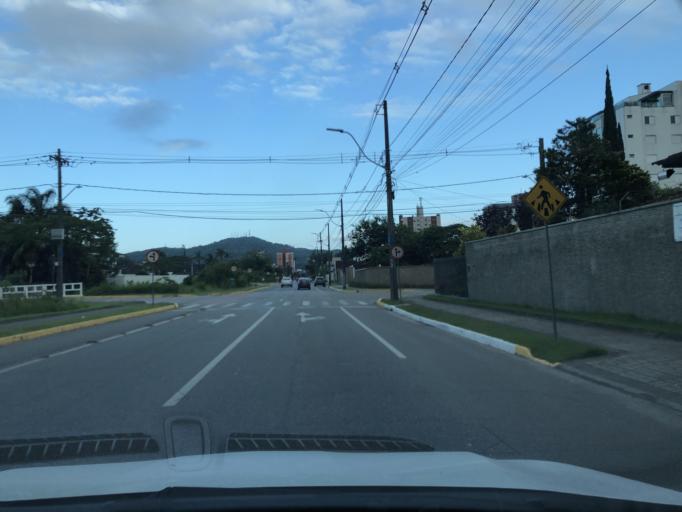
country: BR
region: Santa Catarina
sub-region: Joinville
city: Joinville
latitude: -26.2932
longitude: -48.8582
